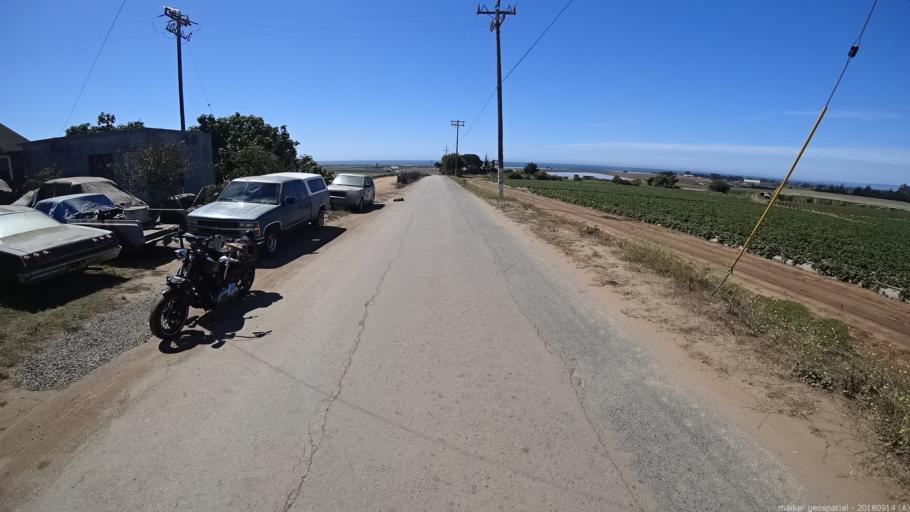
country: US
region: California
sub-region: Monterey County
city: Elkhorn
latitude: 36.8511
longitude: -121.7864
